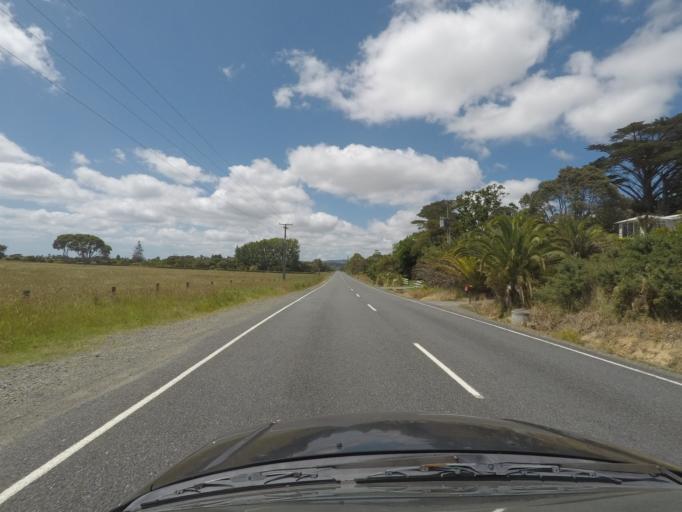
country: NZ
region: Northland
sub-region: Whangarei
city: Ruakaka
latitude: -35.9964
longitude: 174.4727
